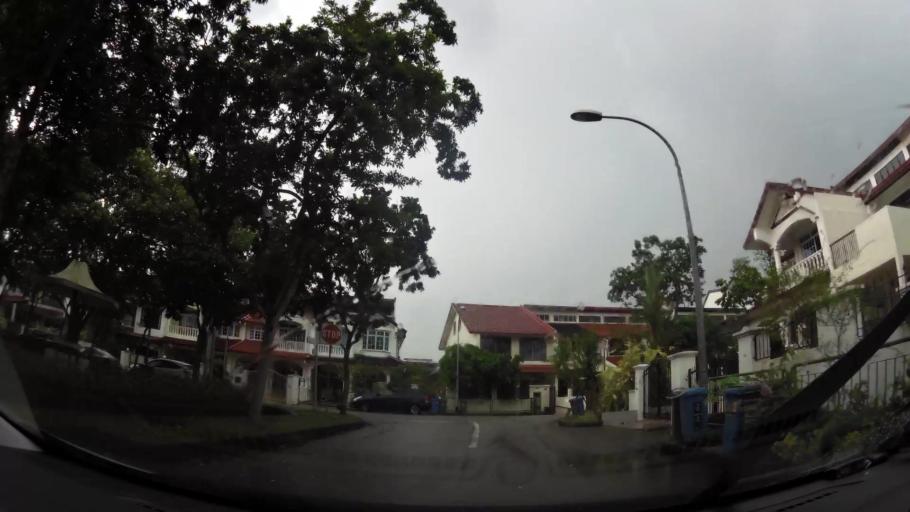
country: MY
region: Johor
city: Kampung Pasir Gudang Baru
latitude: 1.3855
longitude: 103.8372
